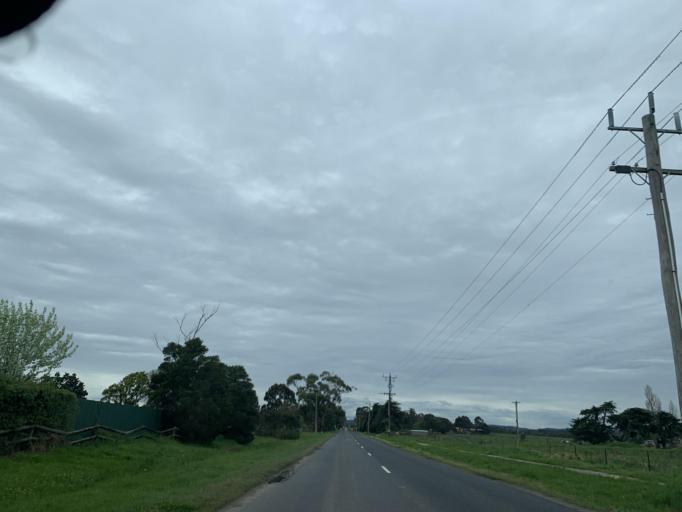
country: AU
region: Victoria
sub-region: Cardinia
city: Pakenham South
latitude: -38.0790
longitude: 145.5707
